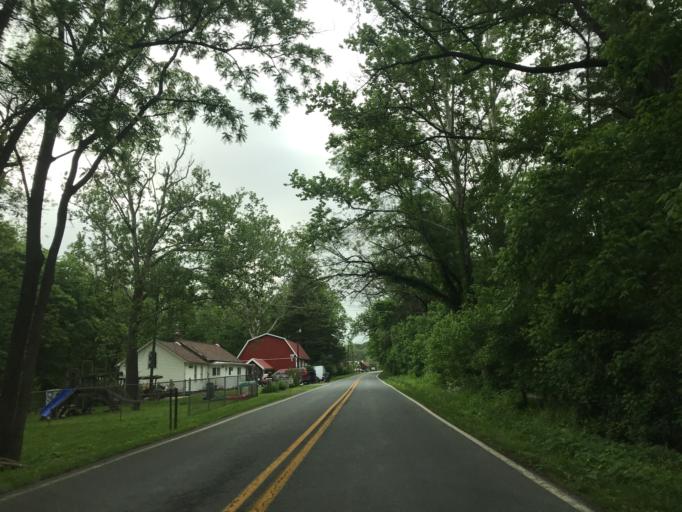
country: US
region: Maryland
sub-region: Frederick County
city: Clover Hill
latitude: 39.4954
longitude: -77.3999
